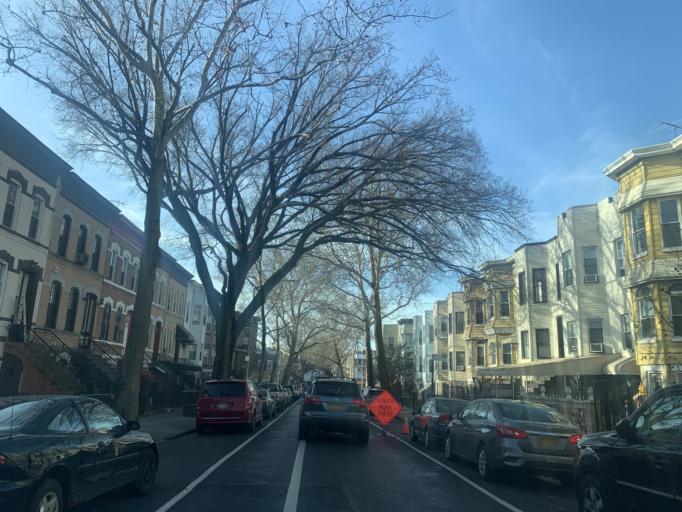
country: US
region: New York
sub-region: Kings County
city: East New York
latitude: 40.6918
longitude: -73.9116
